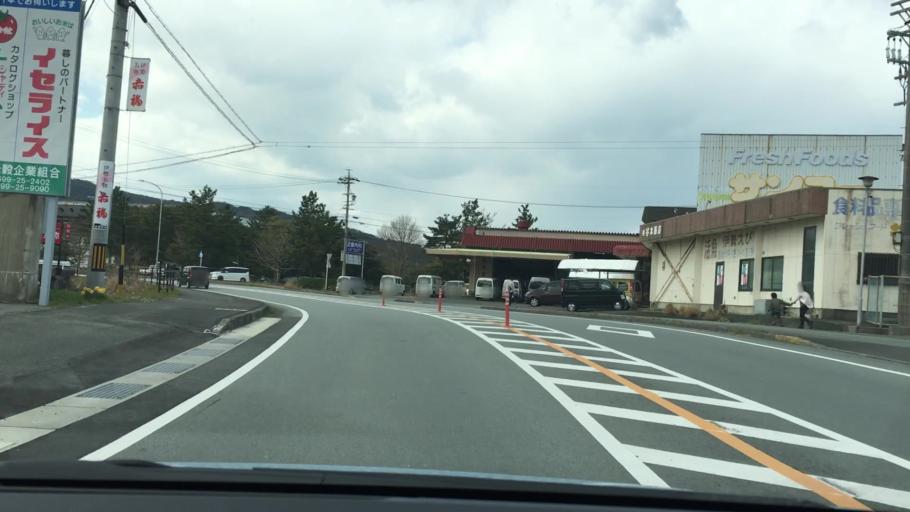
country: JP
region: Mie
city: Toba
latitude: 34.4673
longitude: 136.8536
